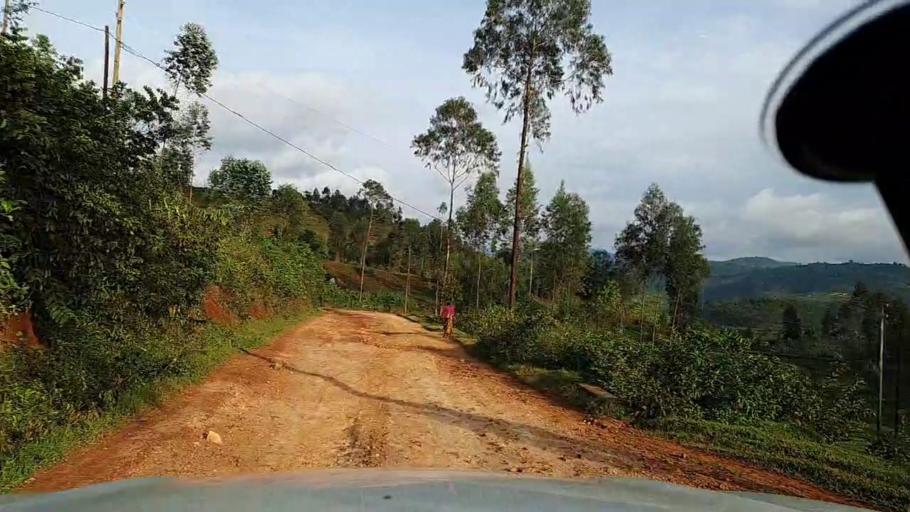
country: RW
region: Southern Province
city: Gitarama
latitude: -2.1893
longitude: 29.5761
